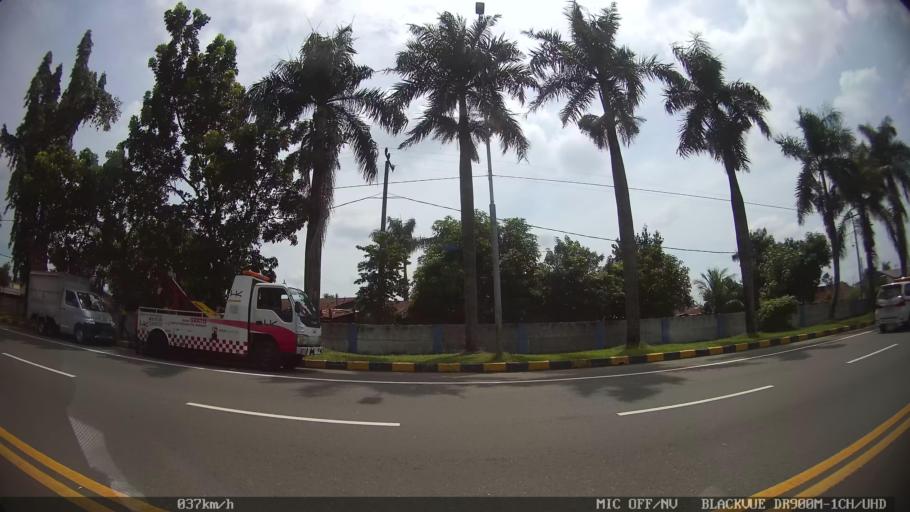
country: ID
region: North Sumatra
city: Medan
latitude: 3.6434
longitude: 98.6813
